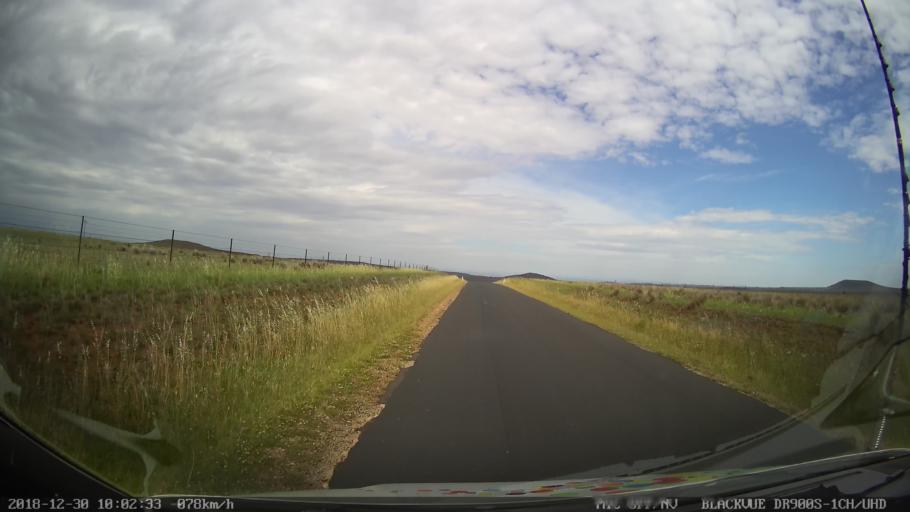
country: AU
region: New South Wales
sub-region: Cooma-Monaro
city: Cooma
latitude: -36.5156
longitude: 149.1700
